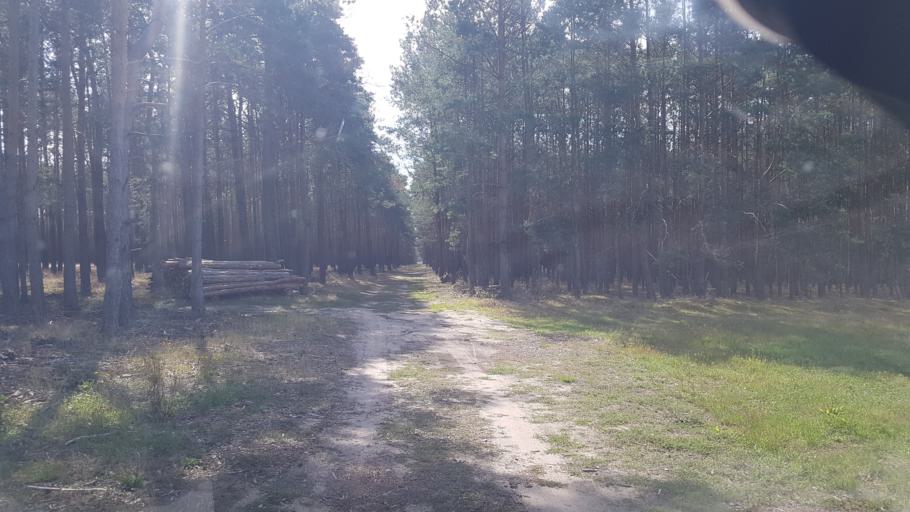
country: DE
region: Brandenburg
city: Sonnewalde
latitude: 51.6577
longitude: 13.6382
